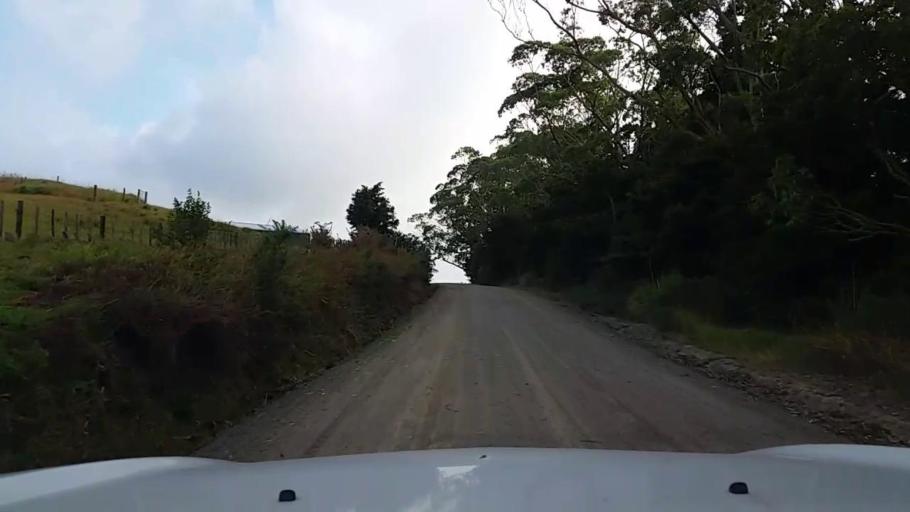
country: NZ
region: Northland
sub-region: Whangarei
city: Maungatapere
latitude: -35.6704
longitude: 174.1750
